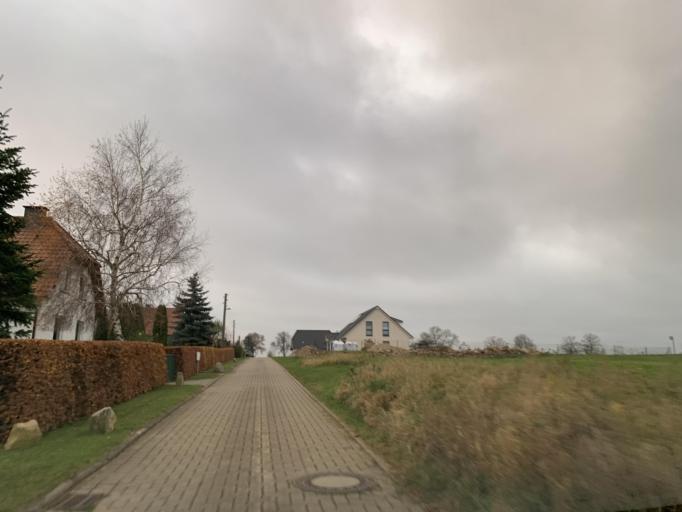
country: DE
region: Mecklenburg-Vorpommern
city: Blankensee
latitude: 53.3940
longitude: 13.3082
